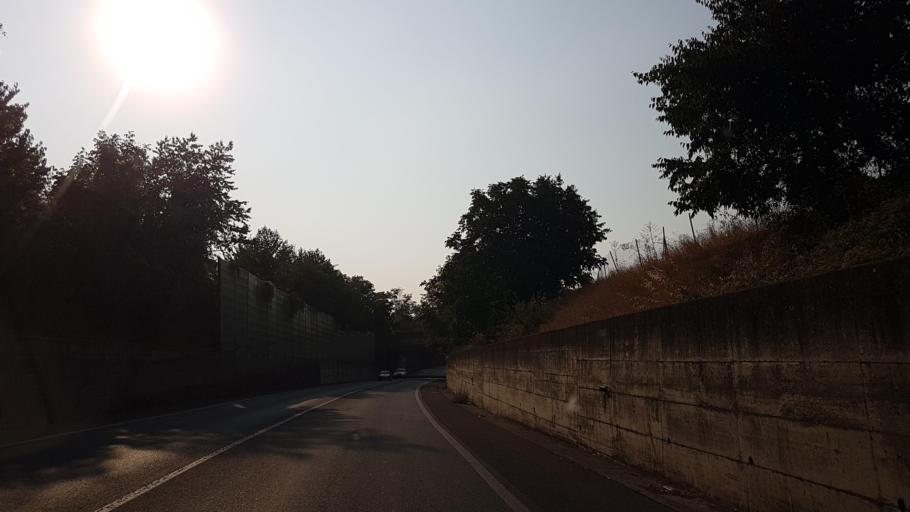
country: IT
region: Emilia-Romagna
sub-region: Provincia di Parma
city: Collecchio
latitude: 44.7573
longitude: 10.2172
